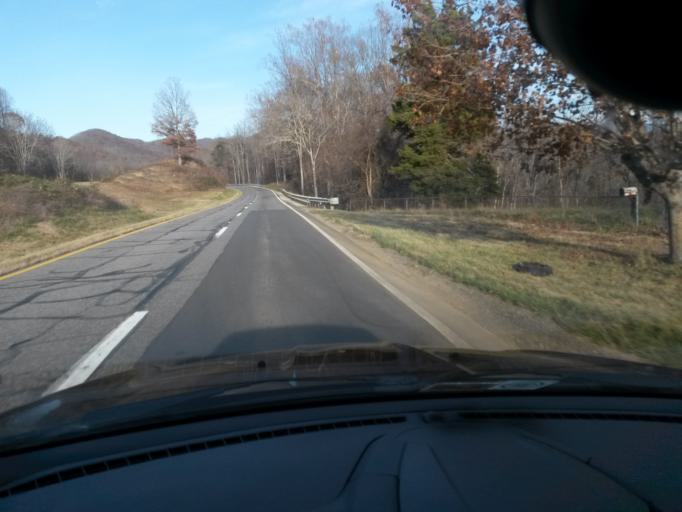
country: US
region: Virginia
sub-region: Botetourt County
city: Fincastle
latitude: 37.6276
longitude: -79.8163
